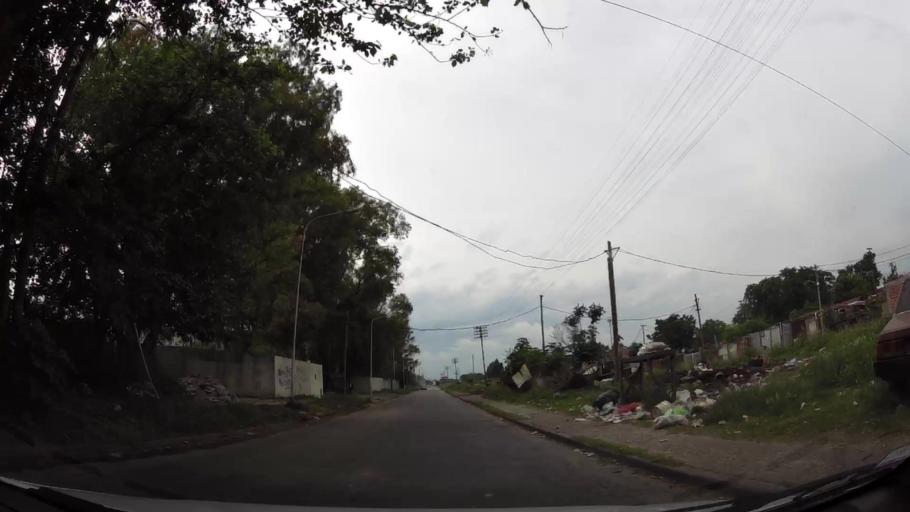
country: AR
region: Buenos Aires
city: San Justo
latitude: -34.6943
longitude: -58.5261
